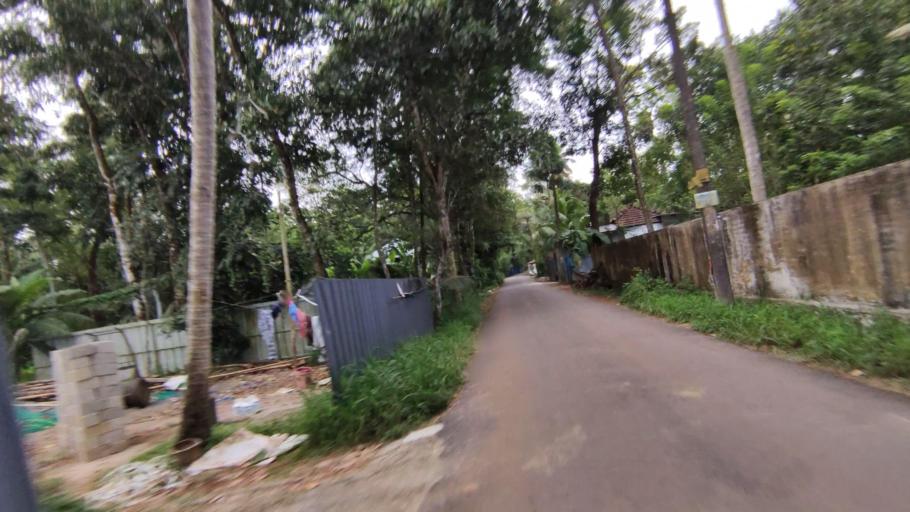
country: IN
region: Kerala
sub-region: Alappuzha
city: Shertallai
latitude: 9.6374
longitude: 76.3602
